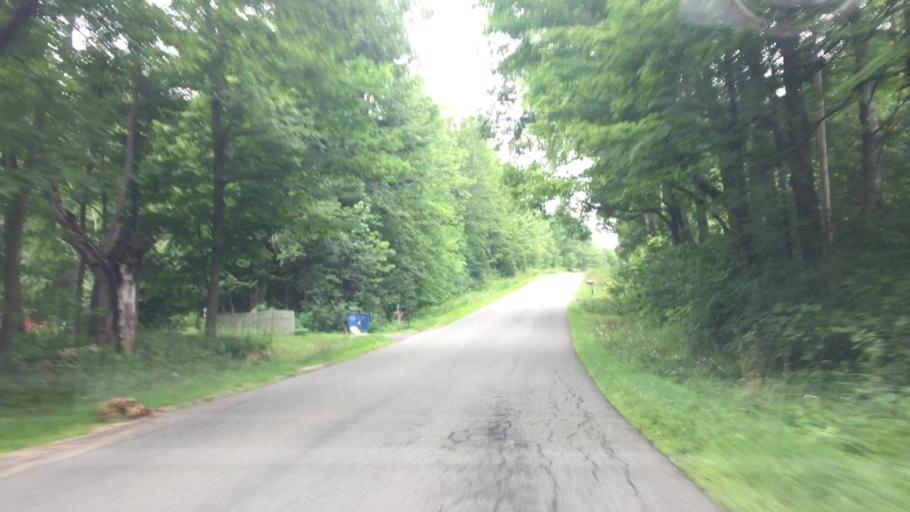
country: US
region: New York
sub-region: Essex County
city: Keeseville
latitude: 44.4524
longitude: -73.5910
